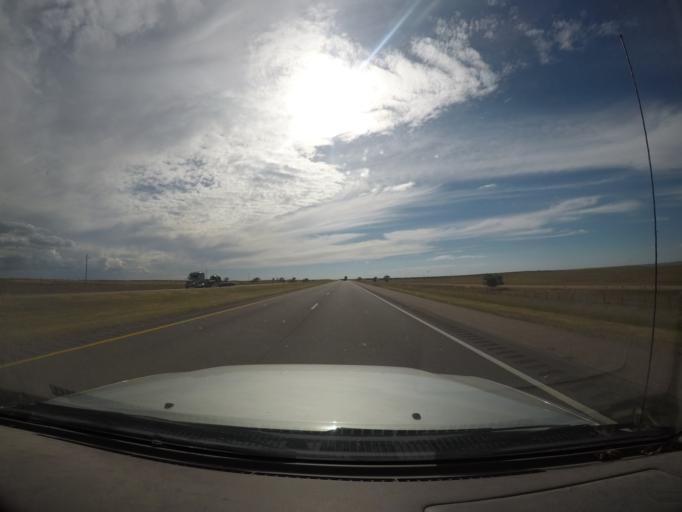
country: US
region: Nebraska
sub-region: Kimball County
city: Kimball
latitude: 41.1920
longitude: -103.8173
